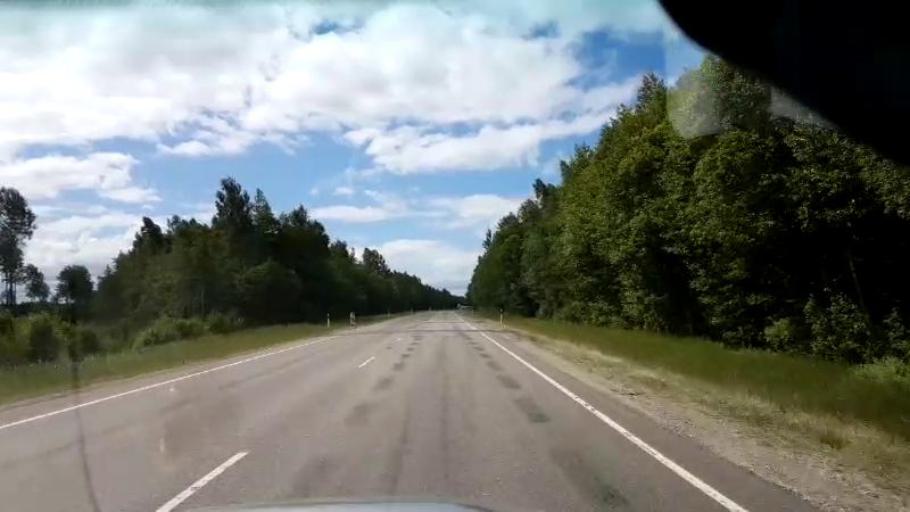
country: LV
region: Salacgrivas
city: Ainazi
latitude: 58.0208
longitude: 24.4990
